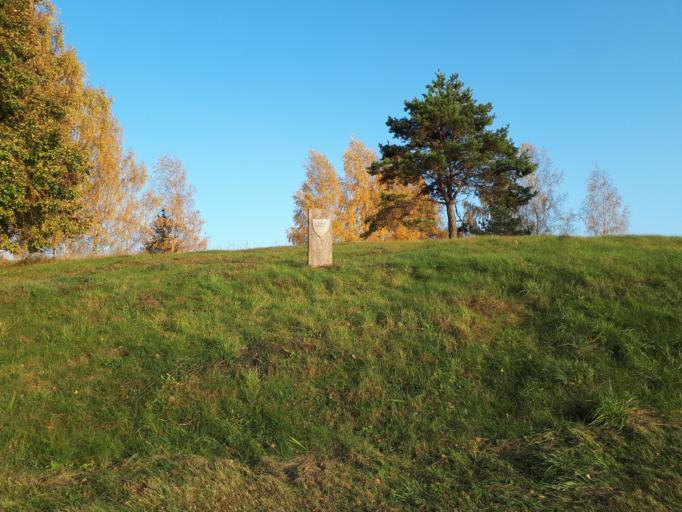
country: LT
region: Alytaus apskritis
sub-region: Alytus
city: Alytus
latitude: 54.2436
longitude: 23.9161
